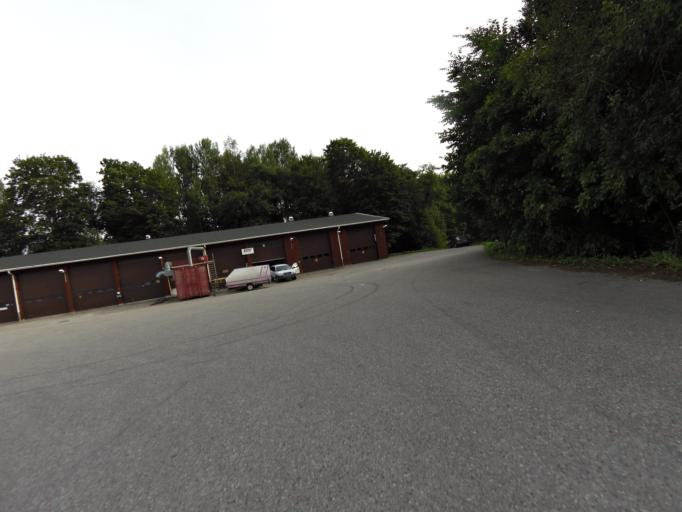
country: SE
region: Gaevleborg
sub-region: Gavle Kommun
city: Gavle
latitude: 60.6981
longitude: 17.1607
